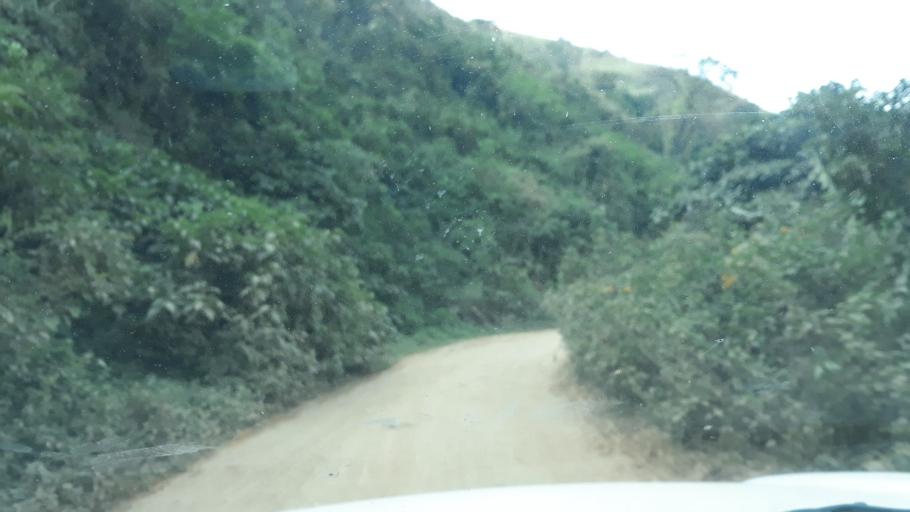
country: RW
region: Western Province
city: Cyangugu
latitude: -2.7142
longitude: 28.9461
